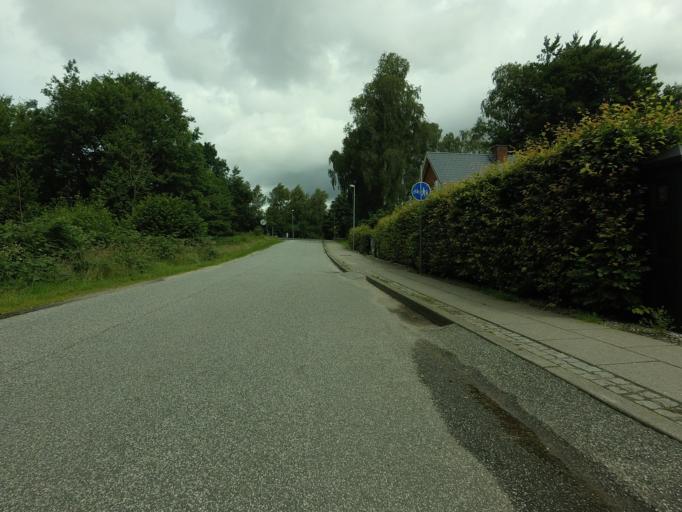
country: DK
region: Central Jutland
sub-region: Randers Kommune
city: Langa
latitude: 56.3907
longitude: 9.9022
